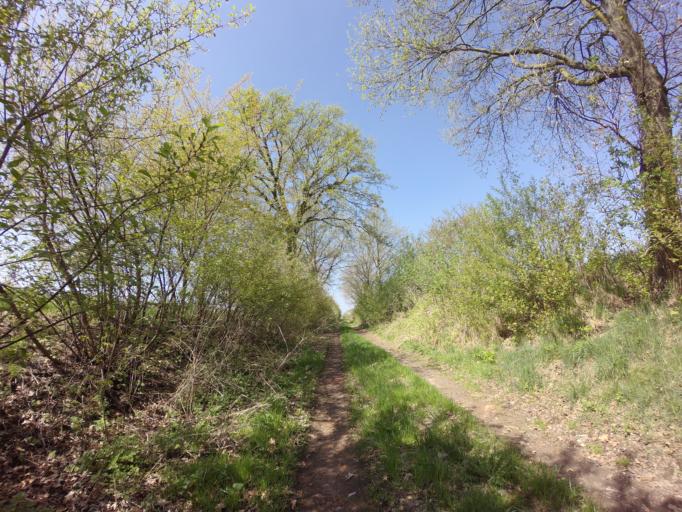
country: PL
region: West Pomeranian Voivodeship
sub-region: Powiat choszczenski
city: Choszczno
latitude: 53.1888
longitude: 15.3860
